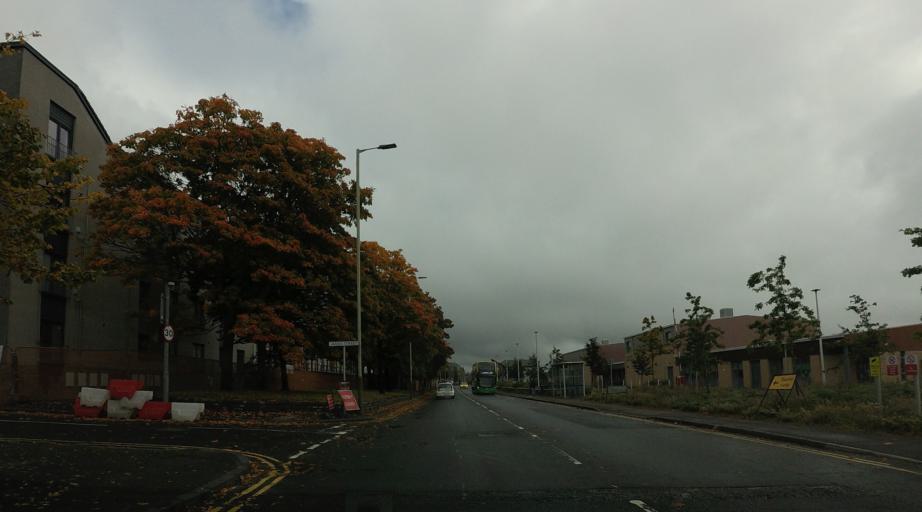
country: GB
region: Scotland
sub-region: Dundee City
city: Dundee
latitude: 56.4683
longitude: -2.9726
